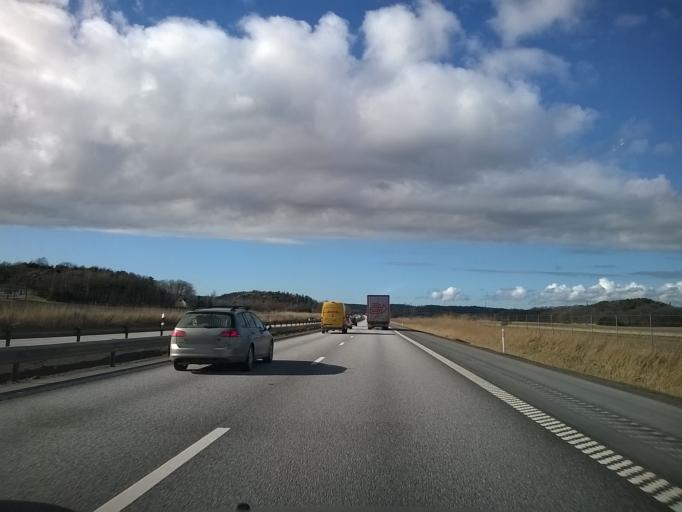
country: SE
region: Halland
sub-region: Kungsbacka Kommun
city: Kungsbacka
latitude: 57.4551
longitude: 12.0898
